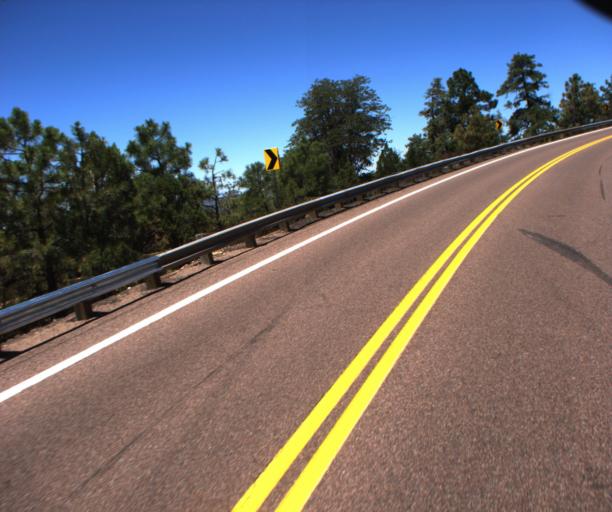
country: US
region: Arizona
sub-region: Gila County
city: Pine
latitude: 34.4220
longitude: -111.5119
